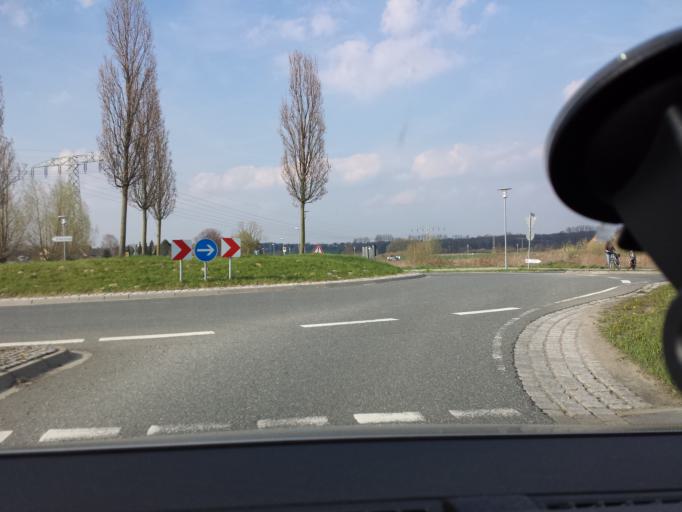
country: DE
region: Lower Saxony
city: Klein Schwulper
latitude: 52.2662
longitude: 10.4482
